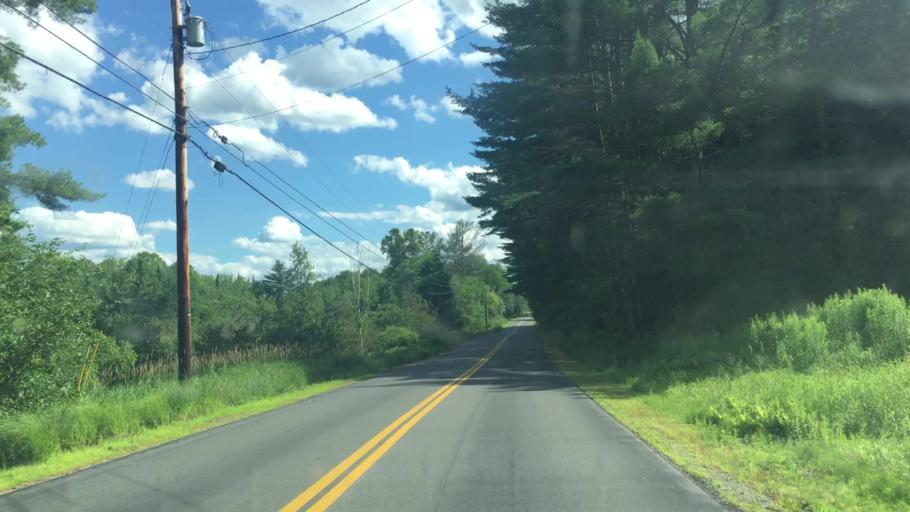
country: US
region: Maine
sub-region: Franklin County
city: Farmington
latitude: 44.6799
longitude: -70.1317
